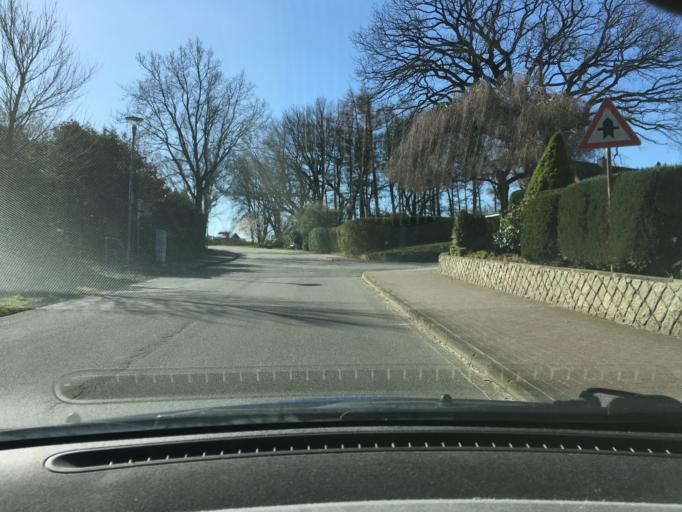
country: DE
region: Schleswig-Holstein
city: Fahrdorf
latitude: 54.5024
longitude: 9.5995
